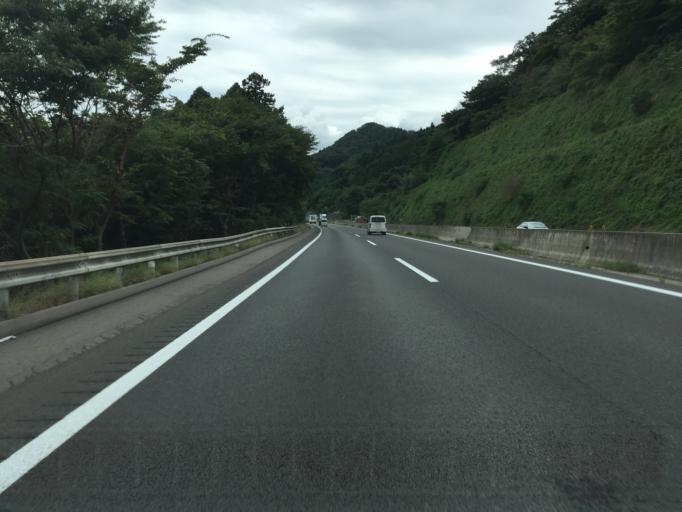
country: JP
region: Fukushima
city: Yanagawamachi-saiwaicho
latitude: 37.9113
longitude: 140.5911
